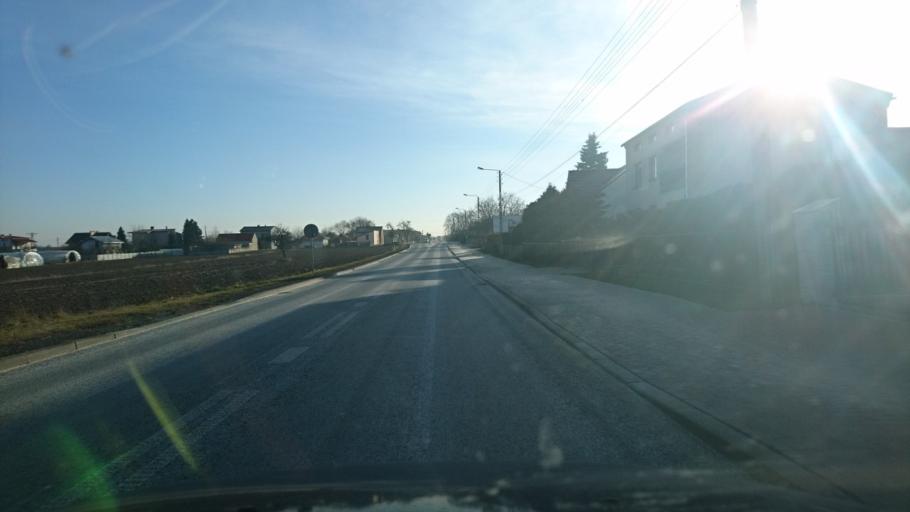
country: PL
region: Silesian Voivodeship
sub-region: Powiat klobucki
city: Starokrzepice
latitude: 51.0188
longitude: 18.6525
